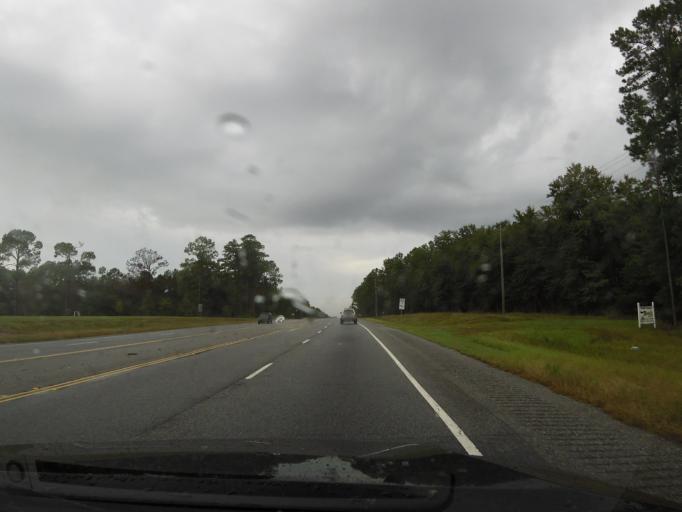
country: US
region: Georgia
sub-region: Wayne County
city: Jesup
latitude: 31.5746
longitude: -81.8459
